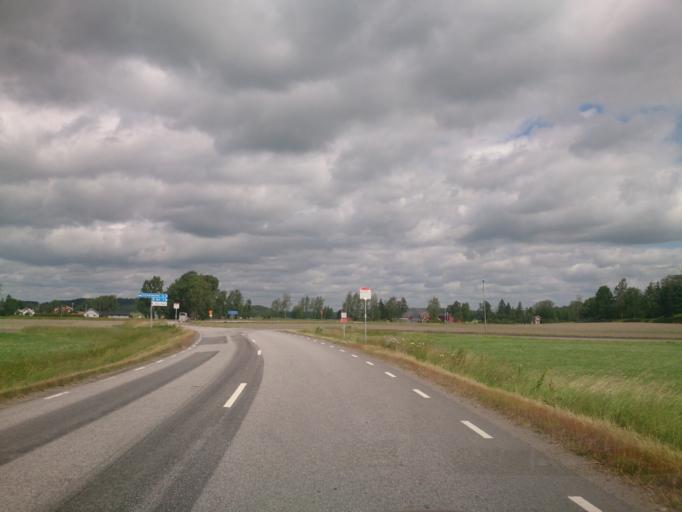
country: SE
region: OEstergoetland
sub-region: Soderkopings Kommun
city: Soederkoeping
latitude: 58.5267
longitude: 16.4712
